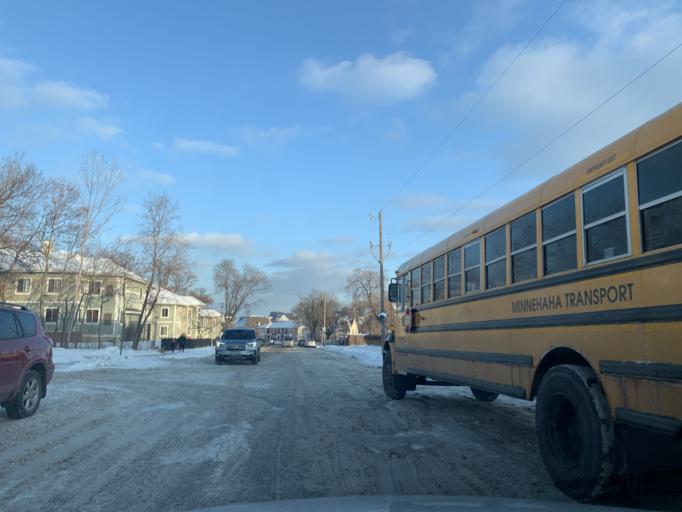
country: US
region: Minnesota
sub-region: Hennepin County
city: Minneapolis
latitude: 44.9852
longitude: -93.2961
